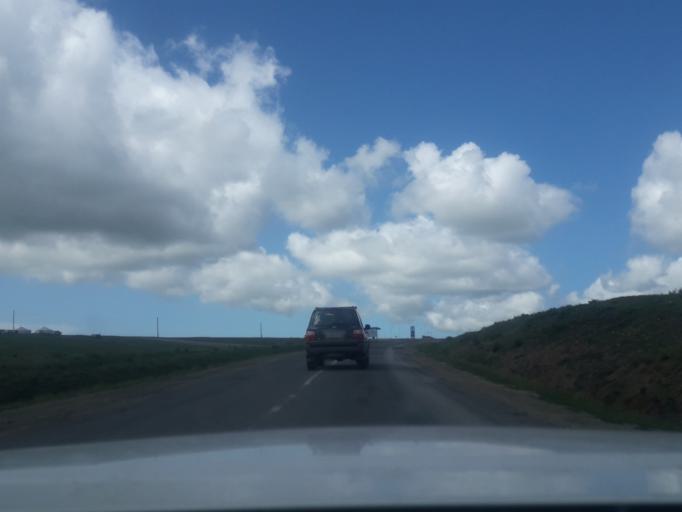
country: MN
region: Central Aimak
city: Ihsueuej
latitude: 48.1315
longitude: 106.4272
